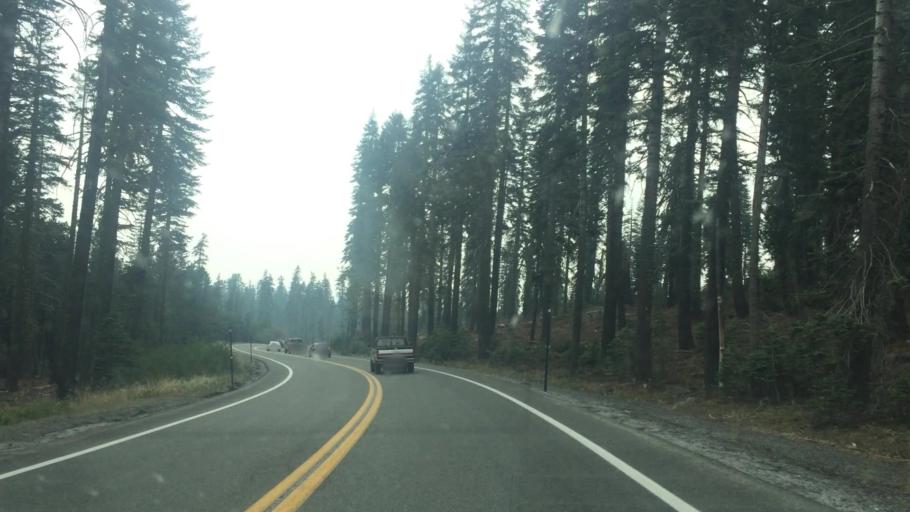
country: US
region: California
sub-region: El Dorado County
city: South Lake Tahoe
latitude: 38.6257
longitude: -120.2148
